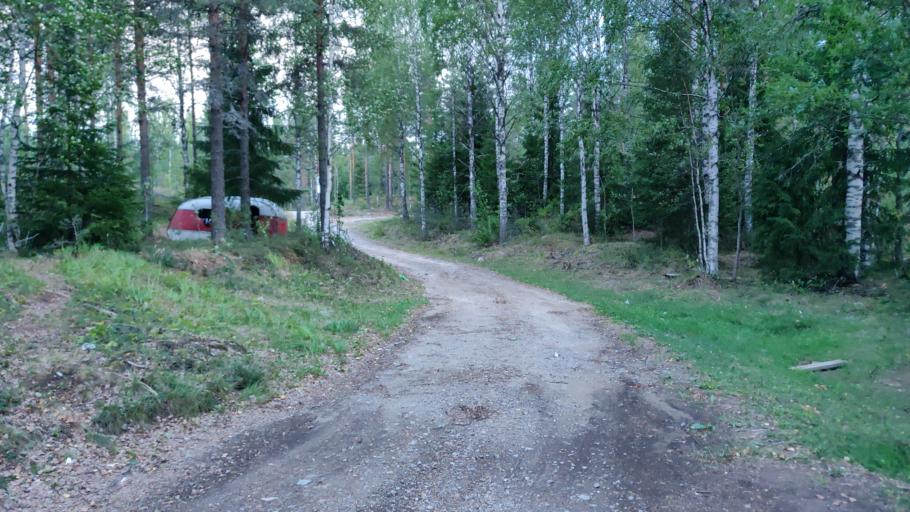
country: NO
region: Hedmark
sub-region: Trysil
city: Innbygda
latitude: 60.9197
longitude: 12.5532
